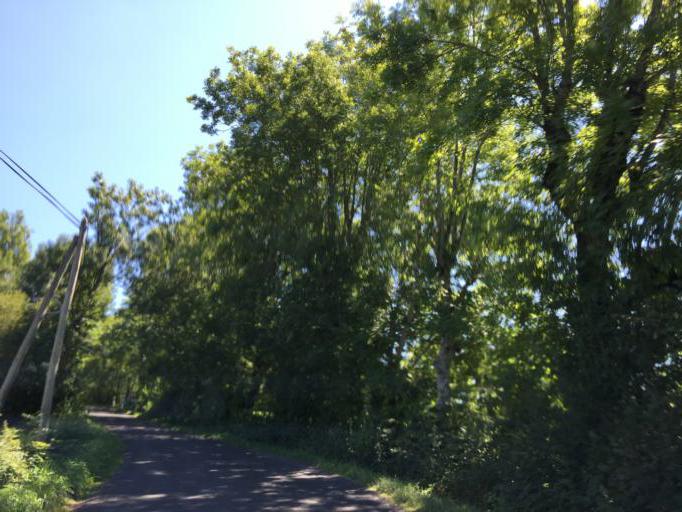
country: FR
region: Midi-Pyrenees
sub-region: Departement de l'Aveyron
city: Laguiole
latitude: 44.6487
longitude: 2.8741
